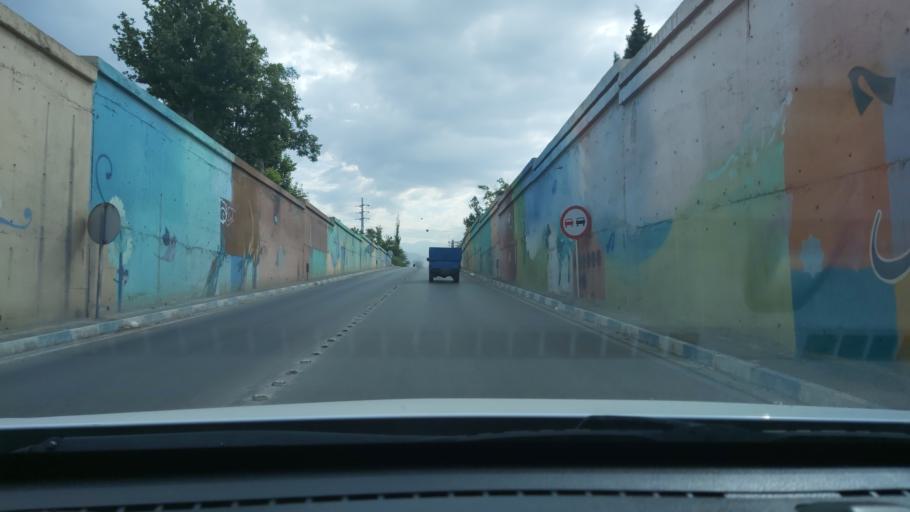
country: IR
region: Alborz
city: Hashtgerd
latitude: 35.9352
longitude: 50.7575
